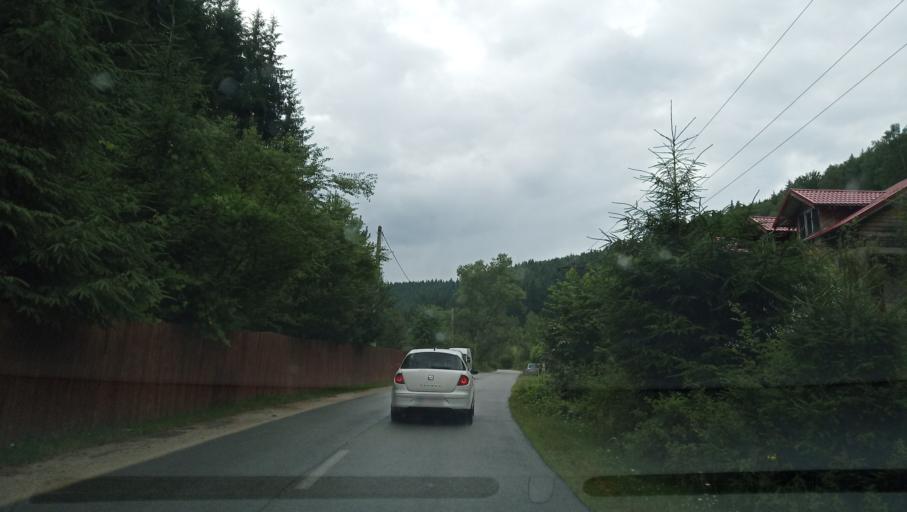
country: RO
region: Hunedoara
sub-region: Oras Petrila
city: Petrila
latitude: 45.3995
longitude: 23.4167
